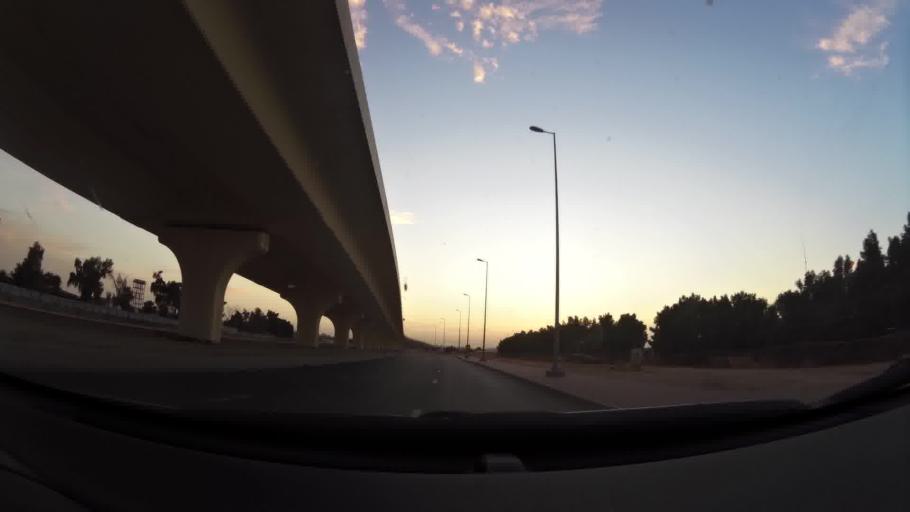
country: KW
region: Al Asimah
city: Ar Rabiyah
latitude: 29.3210
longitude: 47.8857
